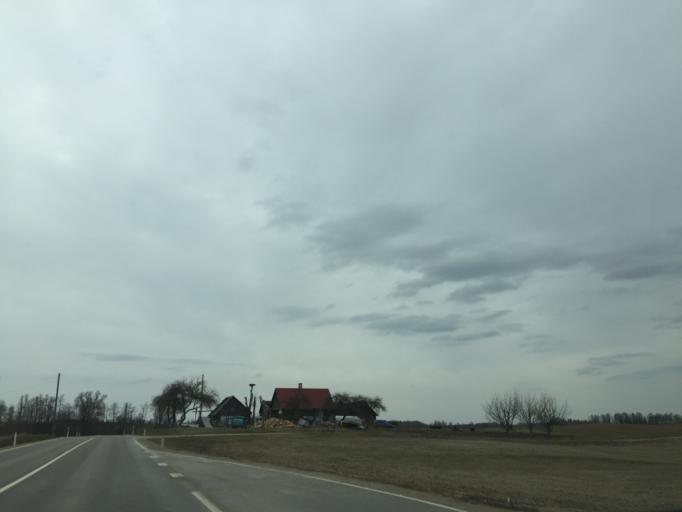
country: LV
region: Ilukste
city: Ilukste
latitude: 55.9975
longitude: 26.2855
